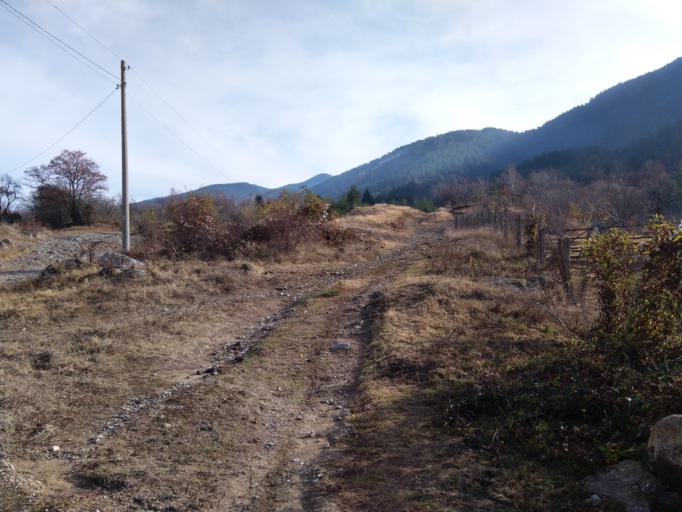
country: BG
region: Kyustendil
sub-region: Obshtina Dupnitsa
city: Dupnitsa
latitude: 42.2410
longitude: 23.1700
